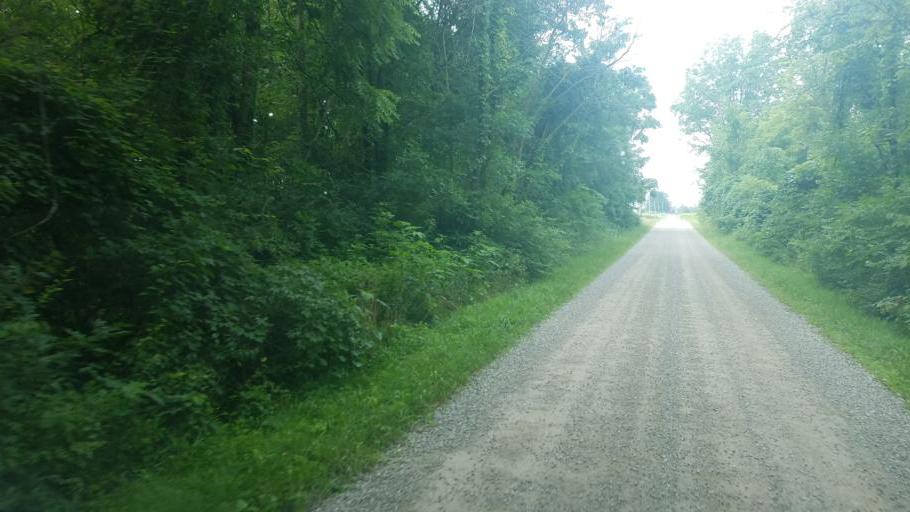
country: US
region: Ohio
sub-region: Delaware County
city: Ashley
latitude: 40.3658
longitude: -82.8842
